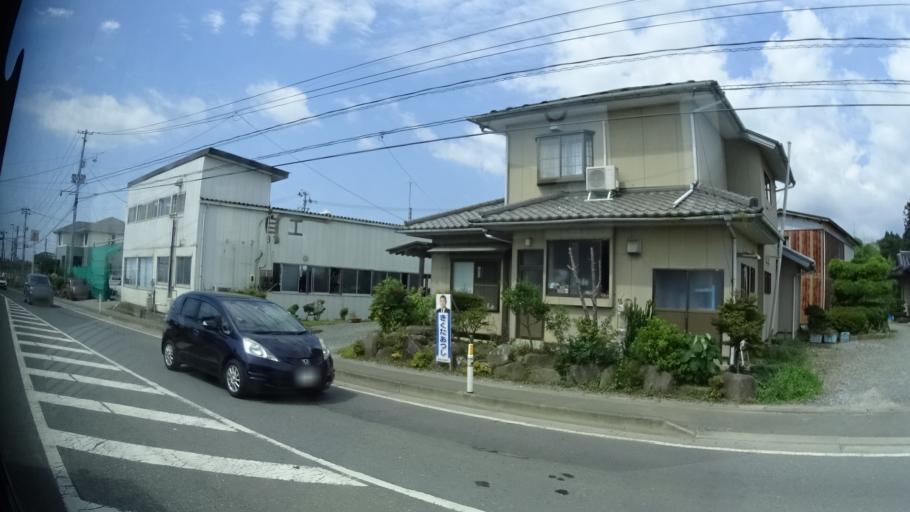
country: JP
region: Iwate
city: Ofunato
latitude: 38.8286
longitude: 141.5771
